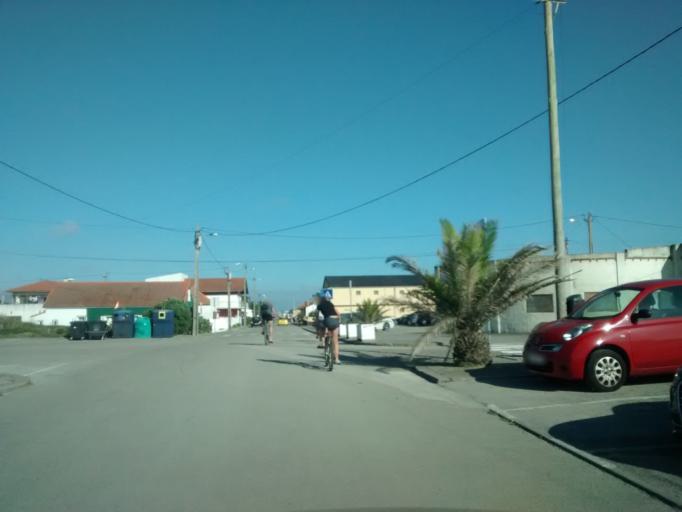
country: PT
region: Aveiro
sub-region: Ilhavo
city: Gafanha da Nazare
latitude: 40.6686
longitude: -8.7427
